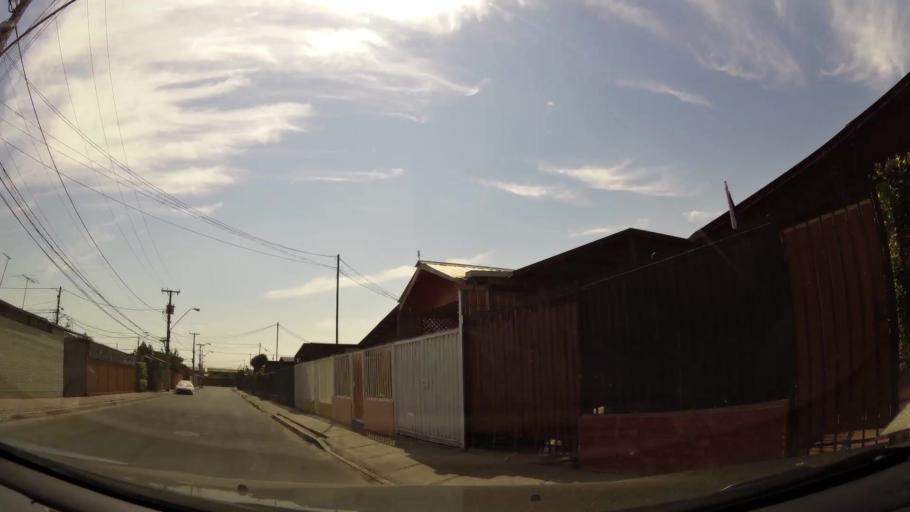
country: CL
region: Santiago Metropolitan
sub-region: Provincia de Cordillera
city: Puente Alto
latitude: -33.5890
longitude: -70.5980
